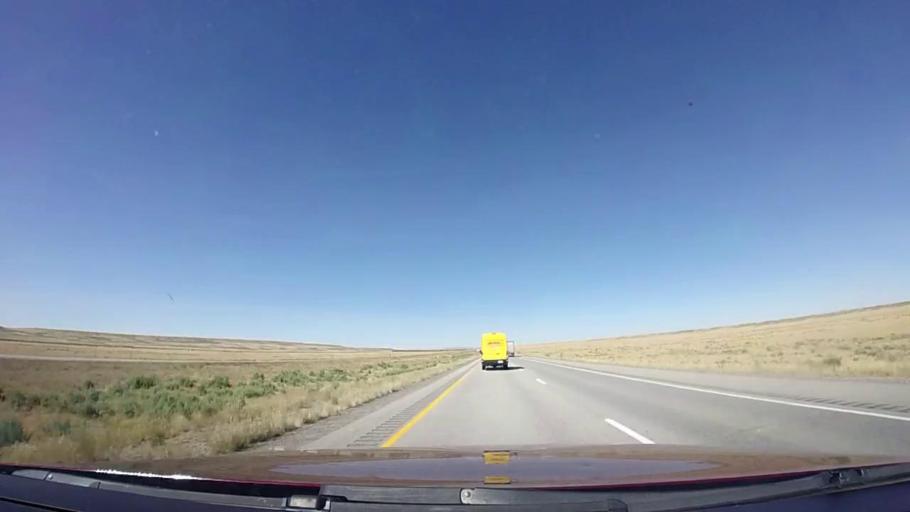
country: US
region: Wyoming
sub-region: Carbon County
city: Rawlins
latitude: 41.6607
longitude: -108.0675
